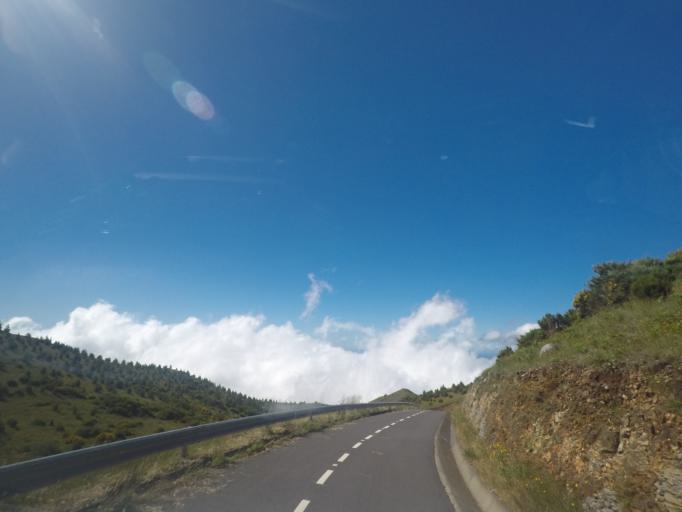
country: PT
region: Madeira
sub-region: Camara de Lobos
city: Curral das Freiras
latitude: 32.7093
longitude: -16.9395
